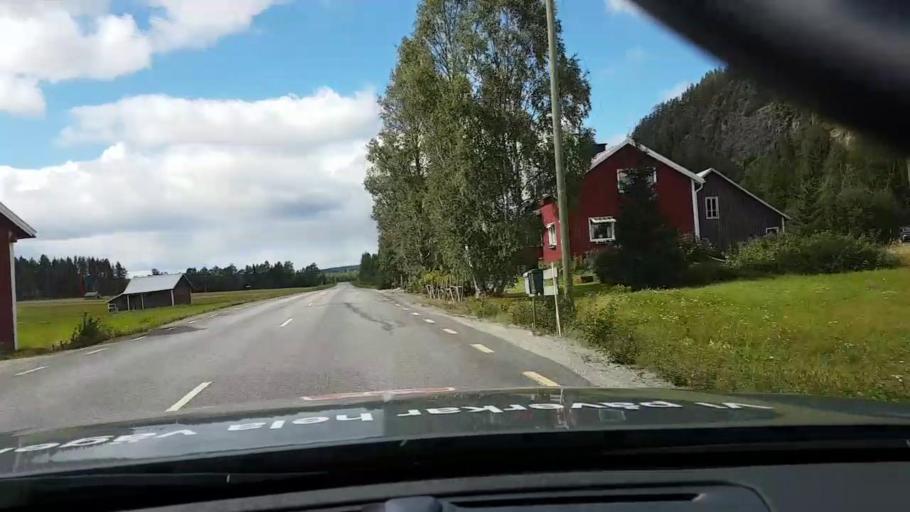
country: SE
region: Vaesternorrland
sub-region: OErnskoeldsviks Kommun
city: Bredbyn
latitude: 63.5271
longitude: 18.0096
